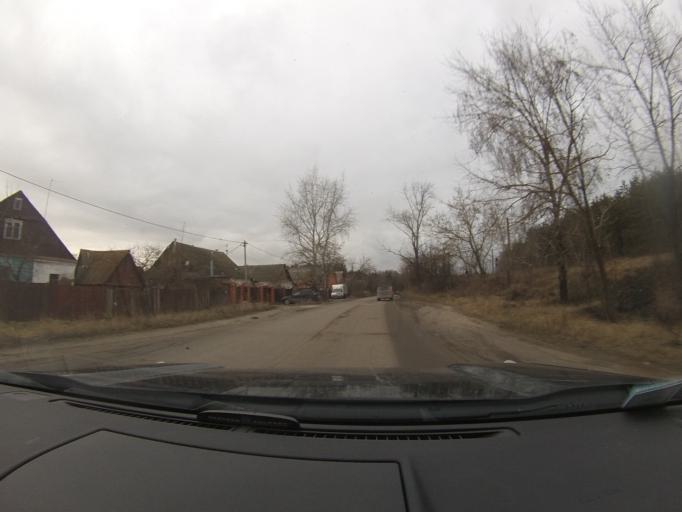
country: RU
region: Moskovskaya
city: Voskresensk
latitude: 55.3306
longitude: 38.6788
